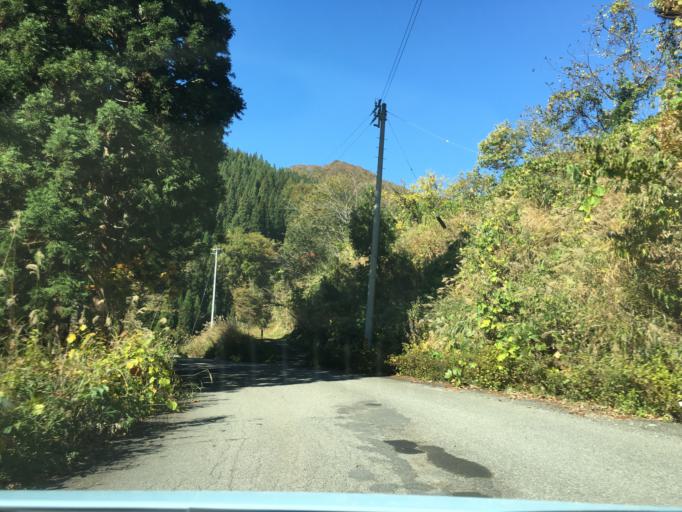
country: JP
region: Fukushima
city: Inawashiro
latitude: 37.4153
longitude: 139.9909
